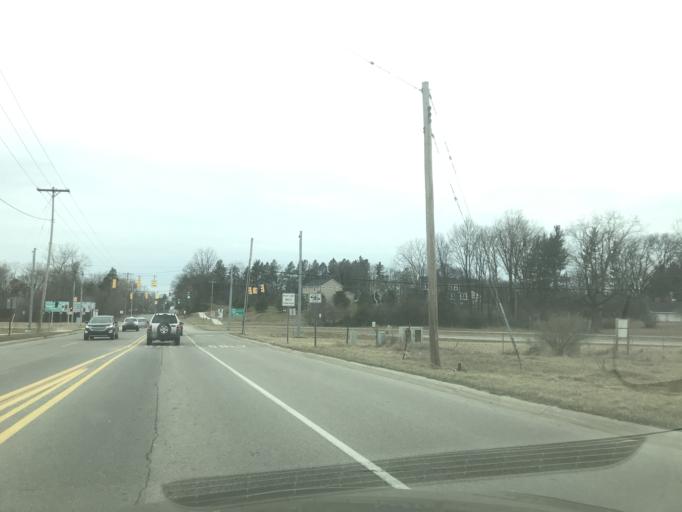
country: US
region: Michigan
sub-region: Ingham County
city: Okemos
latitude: 42.7554
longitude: -84.4408
